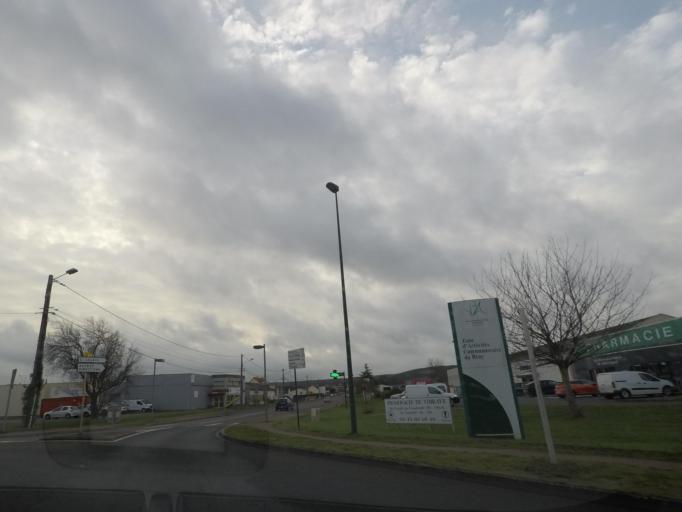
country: FR
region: Pays de la Loire
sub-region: Departement de la Sarthe
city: Vibraye
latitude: 48.0640
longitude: 0.7281
